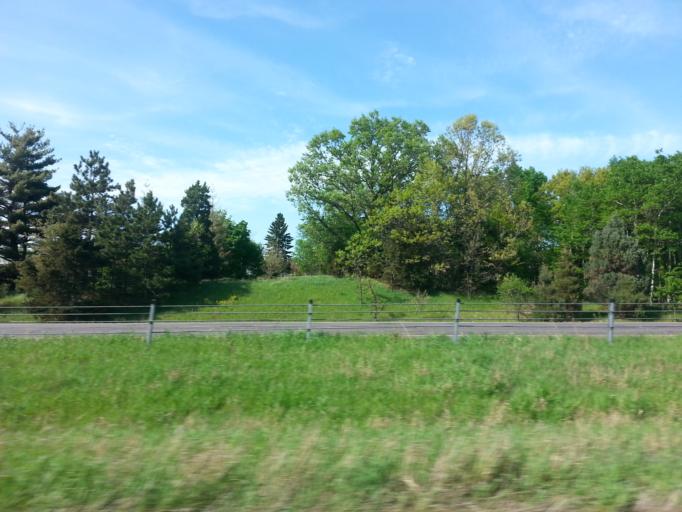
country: US
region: Minnesota
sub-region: Ramsey County
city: North Saint Paul
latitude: 45.0116
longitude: -93.0290
